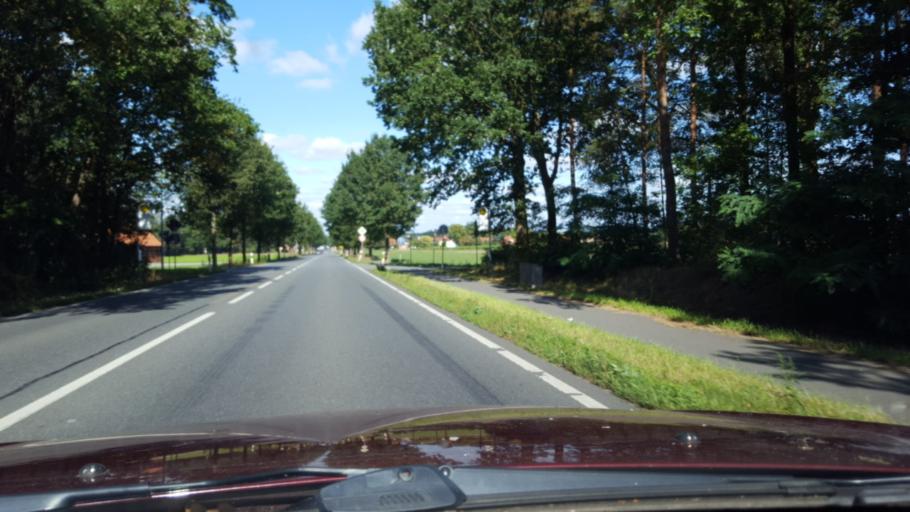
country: DE
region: Lower Saxony
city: Eystrup
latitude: 52.7970
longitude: 9.2112
